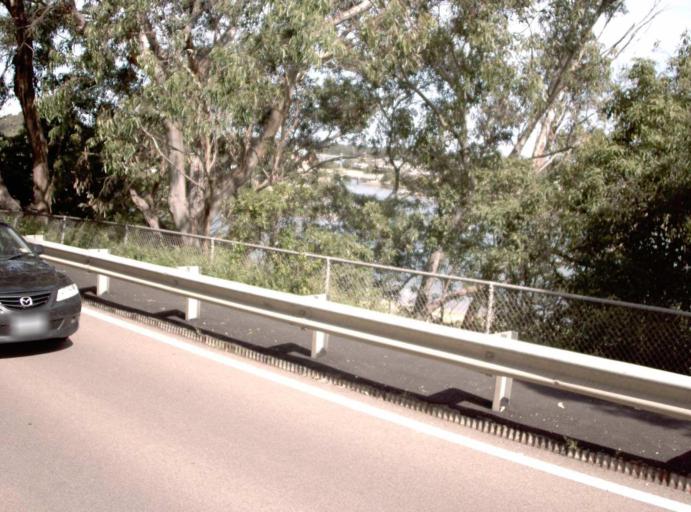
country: AU
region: Victoria
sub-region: East Gippsland
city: Lakes Entrance
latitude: -37.8812
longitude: 147.9683
